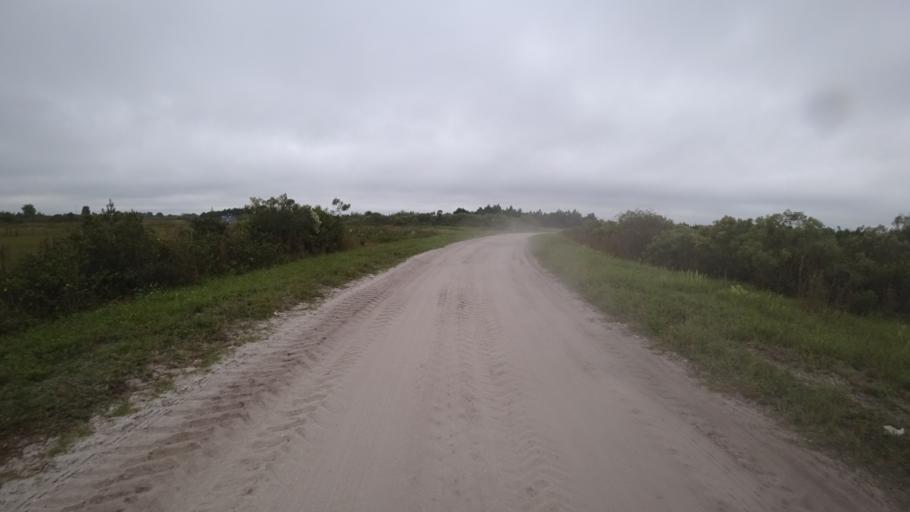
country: US
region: Florida
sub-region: Sarasota County
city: Warm Mineral Springs
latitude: 27.3013
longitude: -82.1359
